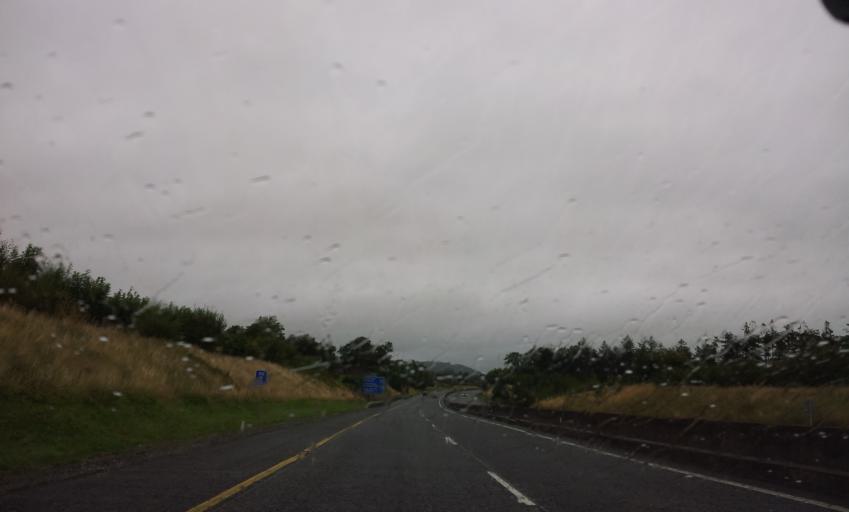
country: IE
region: Munster
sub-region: County Cork
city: Rathcormac
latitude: 52.0711
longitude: -8.3037
